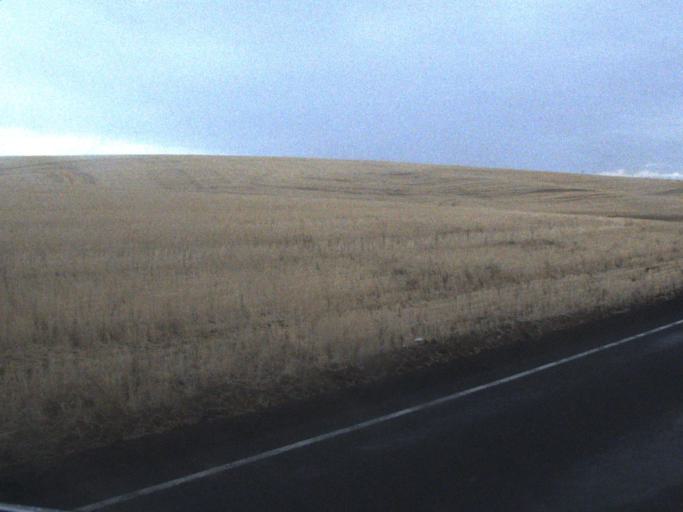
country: US
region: Washington
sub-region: Lincoln County
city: Davenport
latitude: 47.7091
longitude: -118.1482
